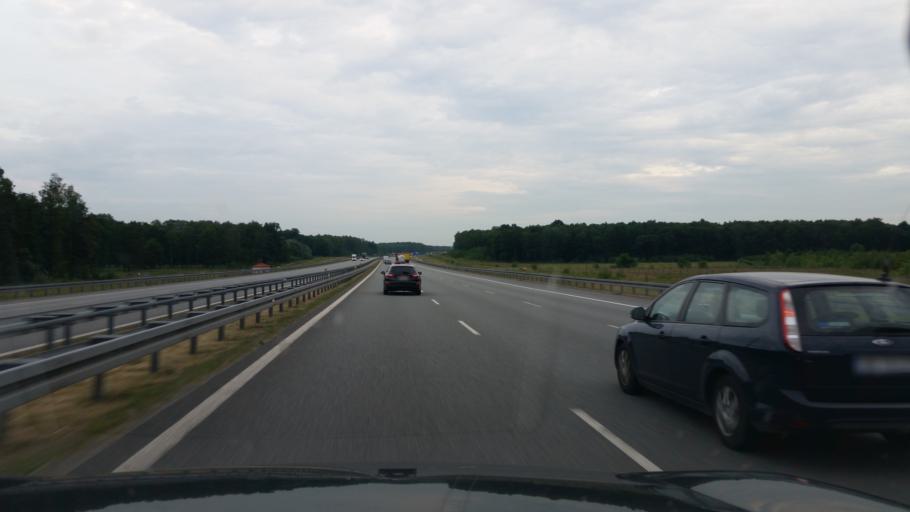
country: PL
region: Silesian Voivodeship
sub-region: Powiat gliwicki
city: Gieraltowice
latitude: 50.2075
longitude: 18.6957
